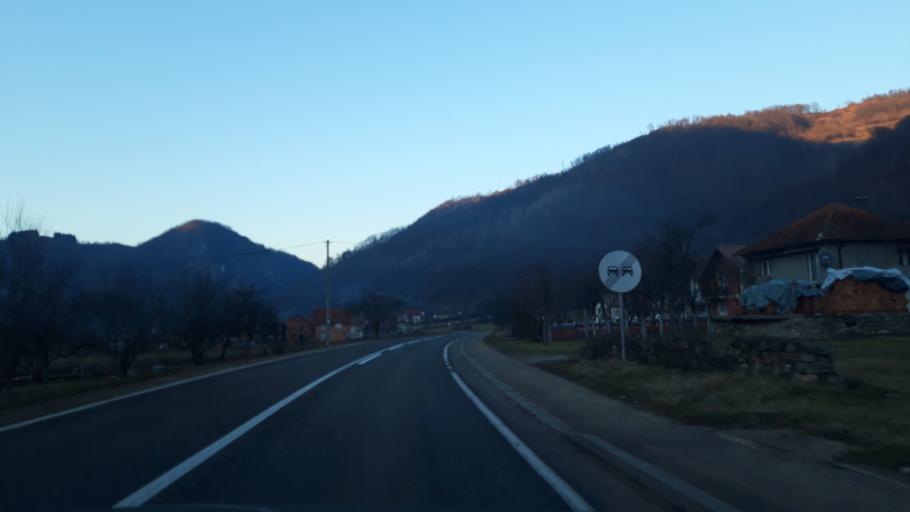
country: BA
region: Republika Srpska
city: Milici
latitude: 44.2534
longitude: 19.1080
